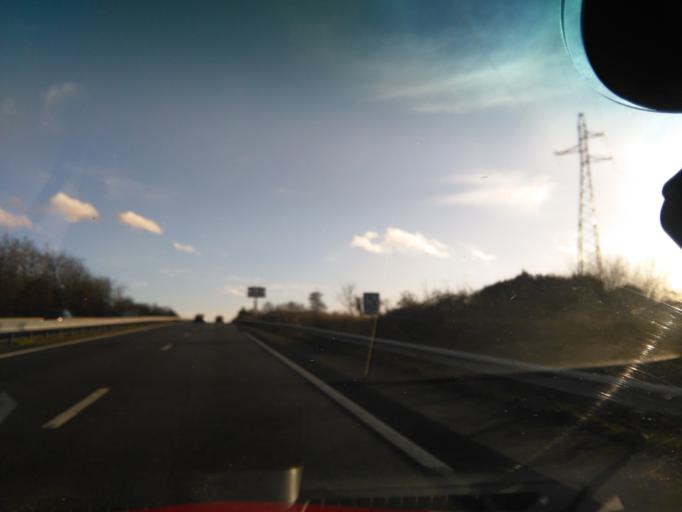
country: FR
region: Lower Normandy
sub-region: Departement du Calvados
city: Falaise
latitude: 48.8986
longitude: -0.2163
